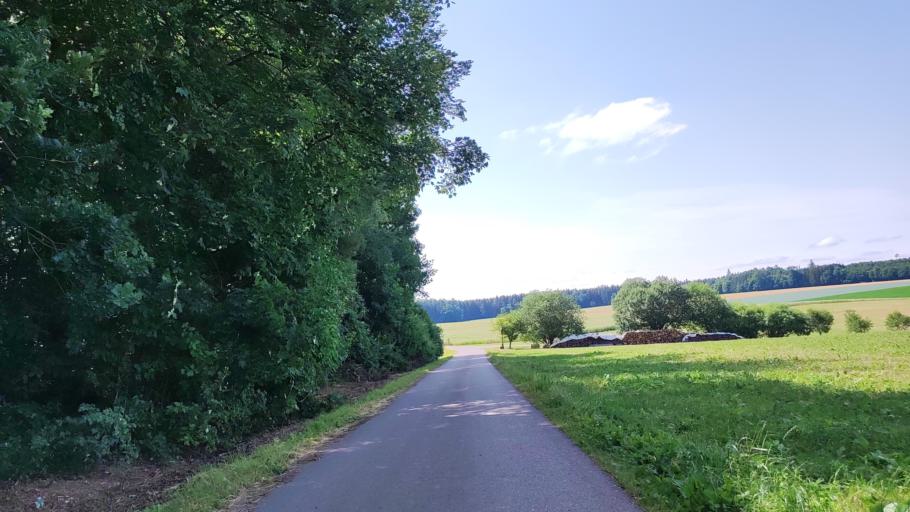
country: DE
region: Bavaria
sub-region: Swabia
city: Holzheim
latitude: 48.4944
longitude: 10.5559
